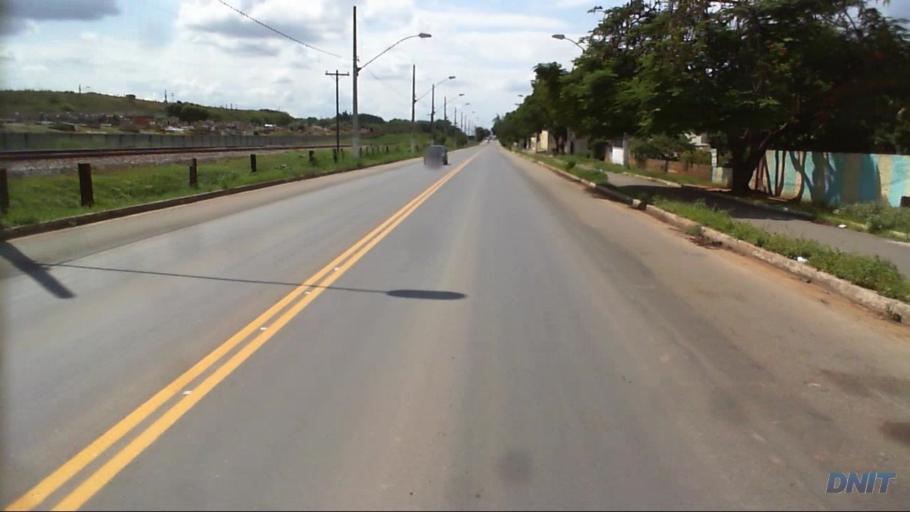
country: BR
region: Minas Gerais
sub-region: Governador Valadares
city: Governador Valadares
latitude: -18.9101
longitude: -41.9949
